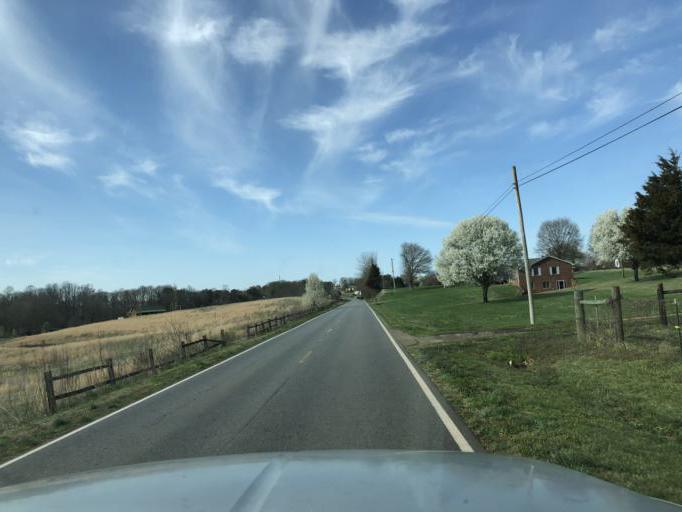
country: US
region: North Carolina
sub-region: Burke County
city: Salem
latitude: 35.5058
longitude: -81.6263
